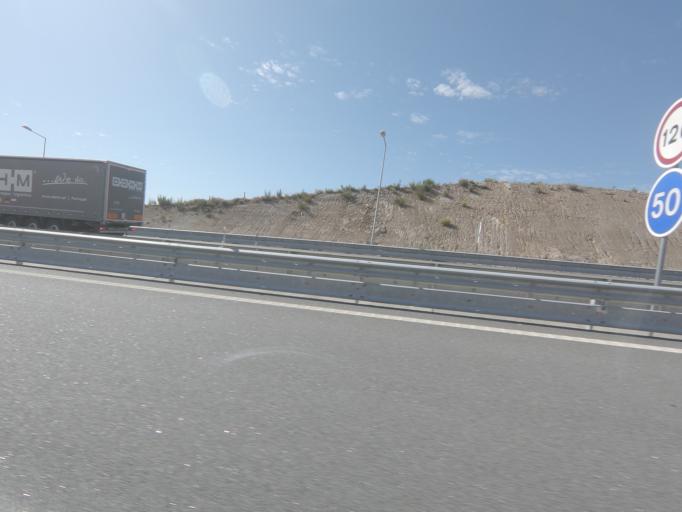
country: PT
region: Vila Real
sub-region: Vila Real
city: Vila Real
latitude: 41.2751
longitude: -7.7724
